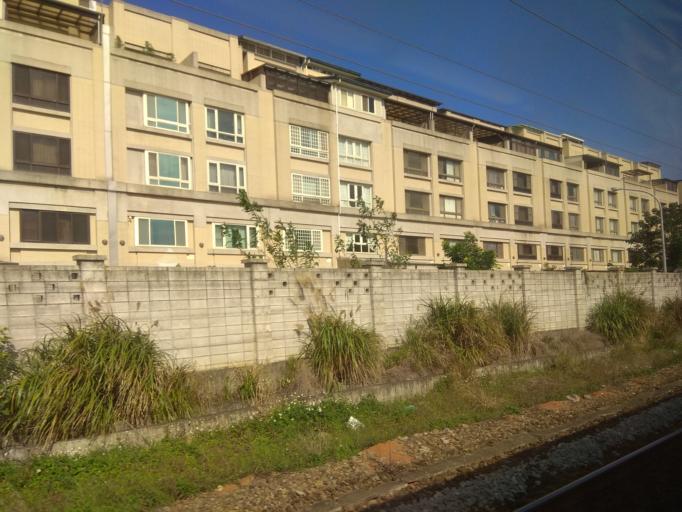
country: TW
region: Taiwan
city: Taoyuan City
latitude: 24.9655
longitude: 121.2472
